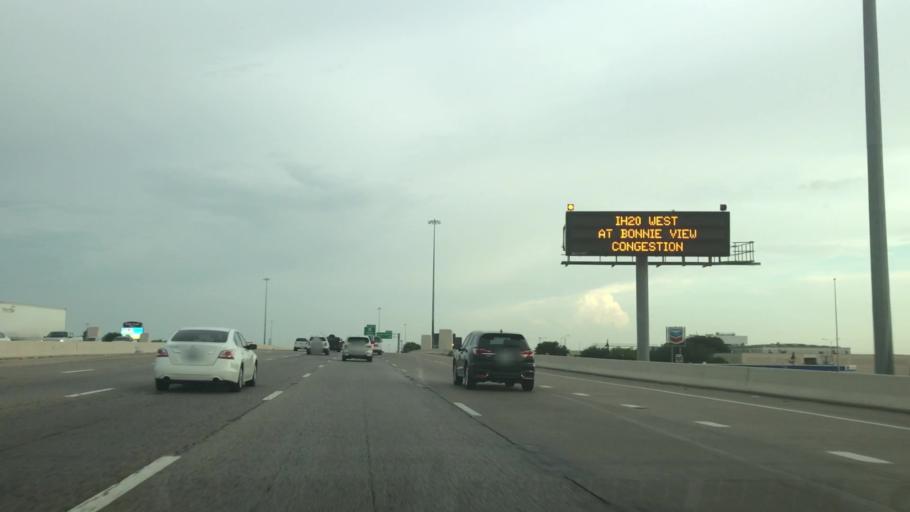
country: US
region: Texas
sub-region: Dallas County
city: Mesquite
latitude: 32.8118
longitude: -96.6281
